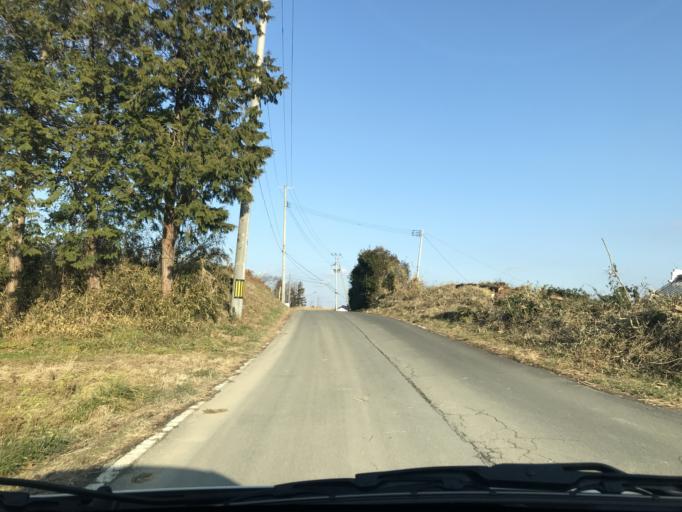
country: JP
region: Miyagi
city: Wakuya
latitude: 38.6947
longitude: 141.1126
